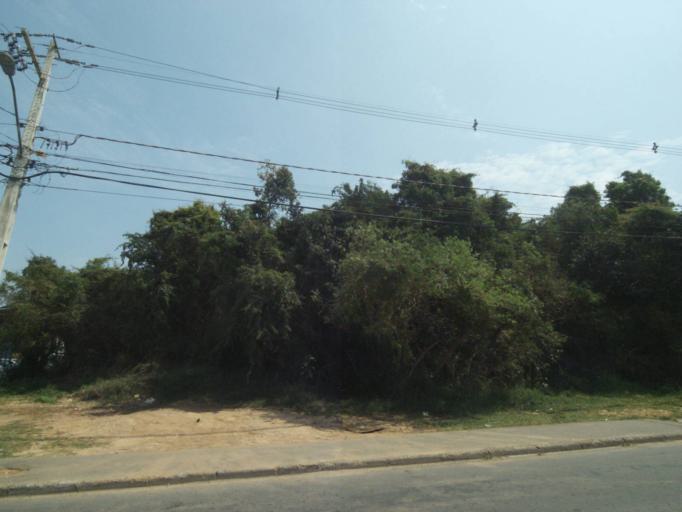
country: BR
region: Parana
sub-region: Curitiba
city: Curitiba
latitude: -25.4775
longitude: -49.3319
